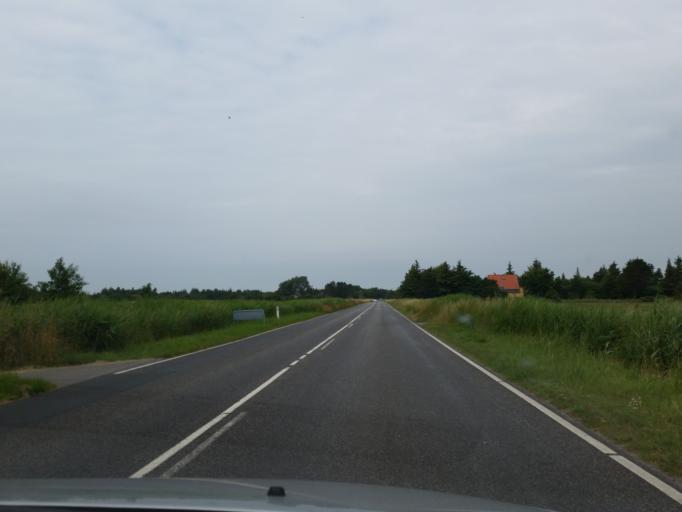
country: DE
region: Schleswig-Holstein
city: List
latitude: 55.1349
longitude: 8.5496
